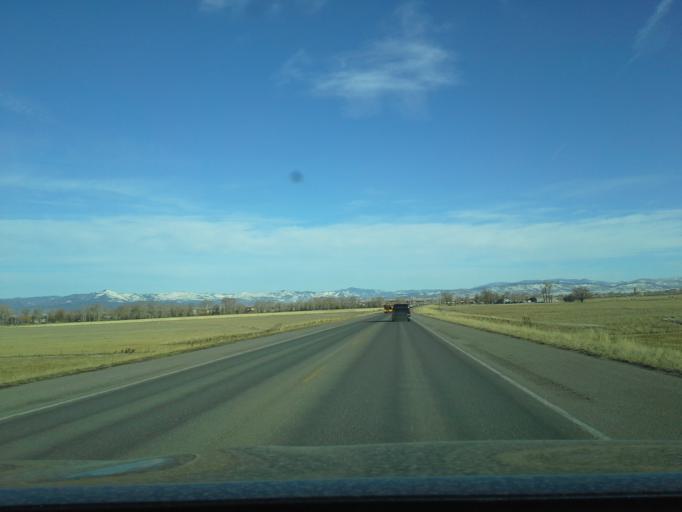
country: US
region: Montana
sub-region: Lewis and Clark County
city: Helena Valley Southeast
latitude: 46.6166
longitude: -111.9746
